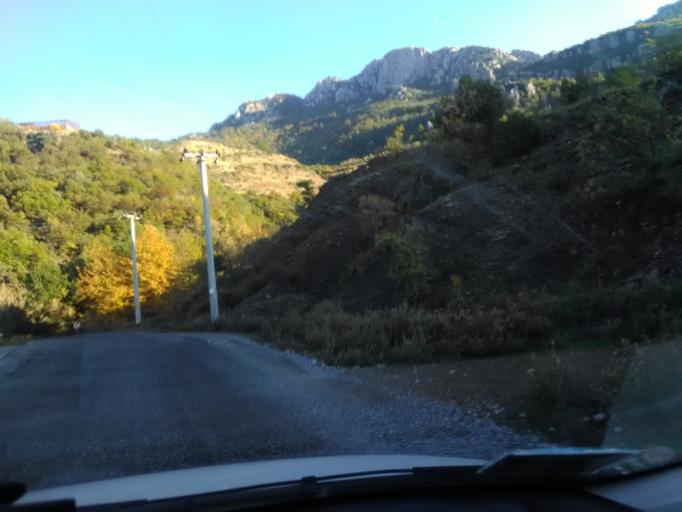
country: TR
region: Antalya
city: Gazipasa
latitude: 36.3084
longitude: 32.4083
